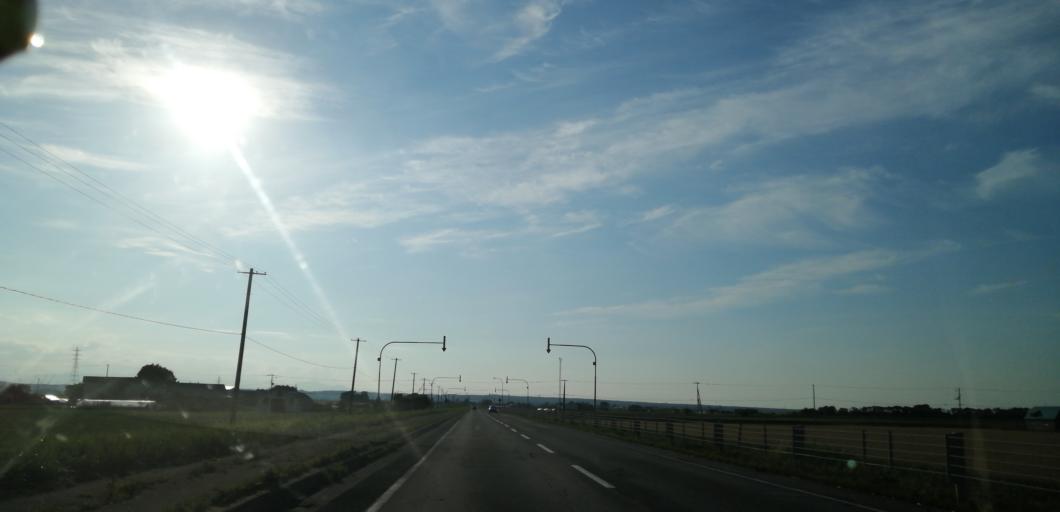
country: JP
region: Hokkaido
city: Kitahiroshima
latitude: 42.9907
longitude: 141.6060
